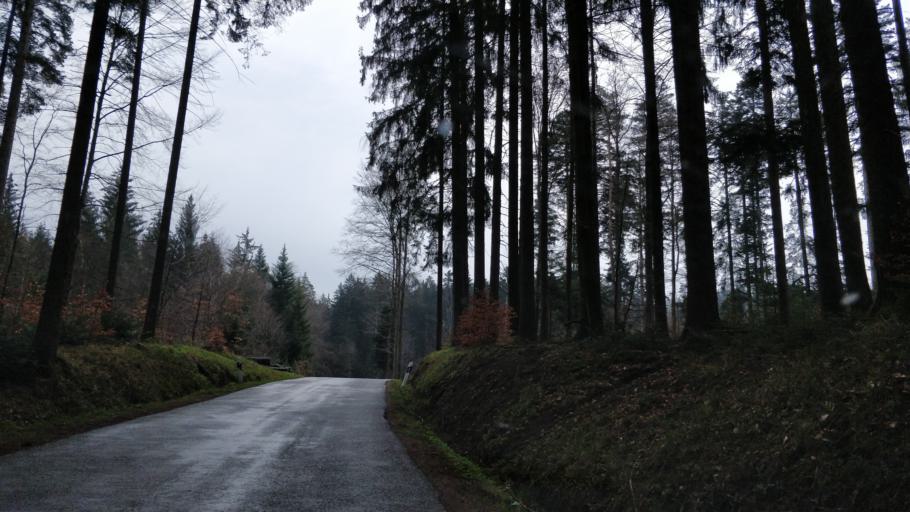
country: DE
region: Baden-Wuerttemberg
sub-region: Regierungsbezirk Stuttgart
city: Murrhardt
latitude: 49.0295
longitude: 9.5996
